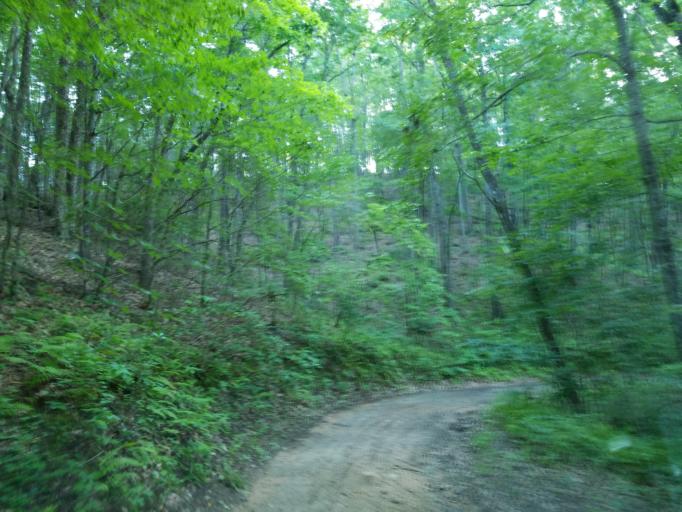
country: US
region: Georgia
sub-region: Fannin County
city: Blue Ridge
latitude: 34.8081
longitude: -84.1620
